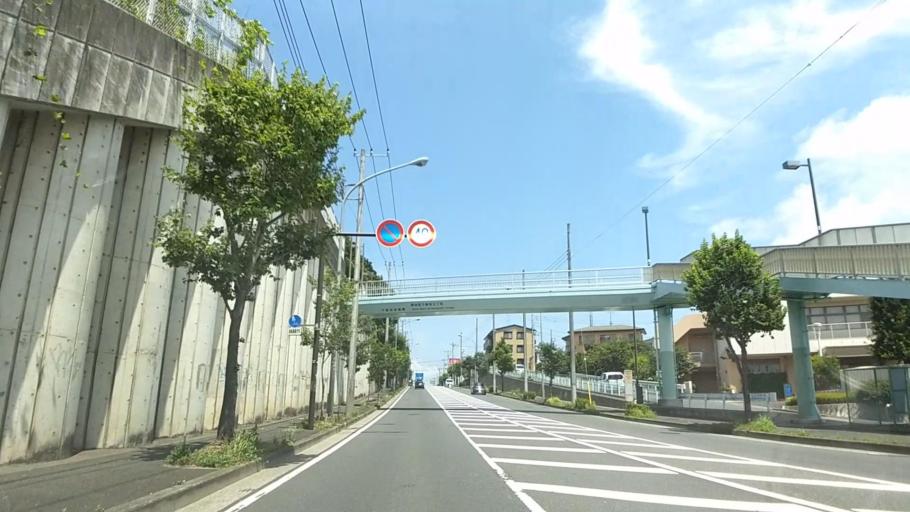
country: JP
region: Kanagawa
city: Minami-rinkan
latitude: 35.4539
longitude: 139.4823
